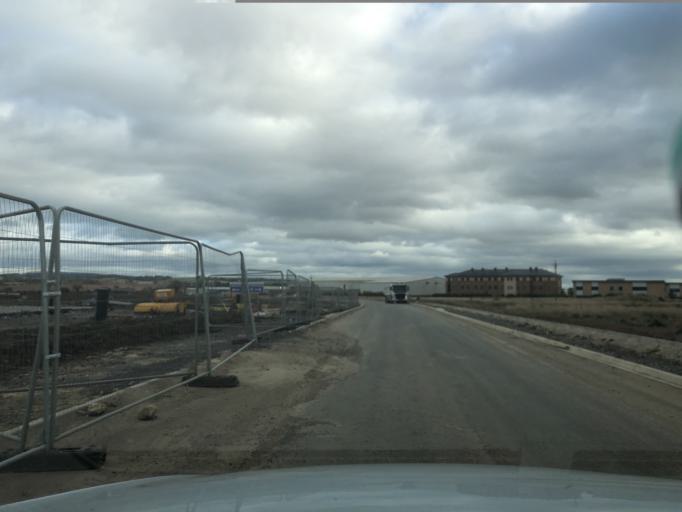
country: GB
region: England
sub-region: North Yorkshire
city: Northallerton
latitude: 54.3526
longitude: -1.4449
